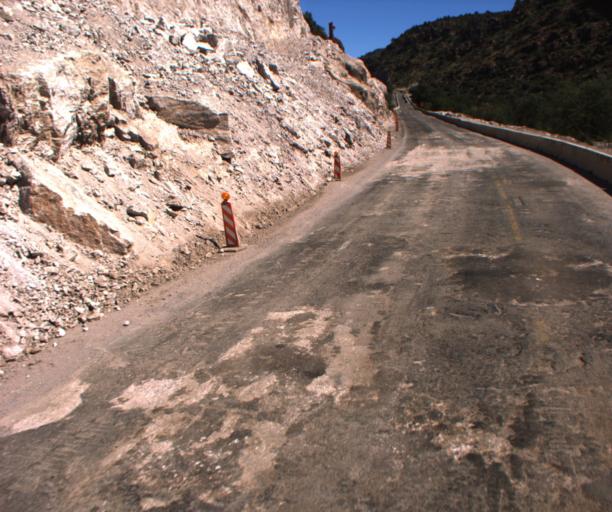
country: US
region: Arizona
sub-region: Pinal County
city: Superior
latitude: 33.3228
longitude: -111.0335
